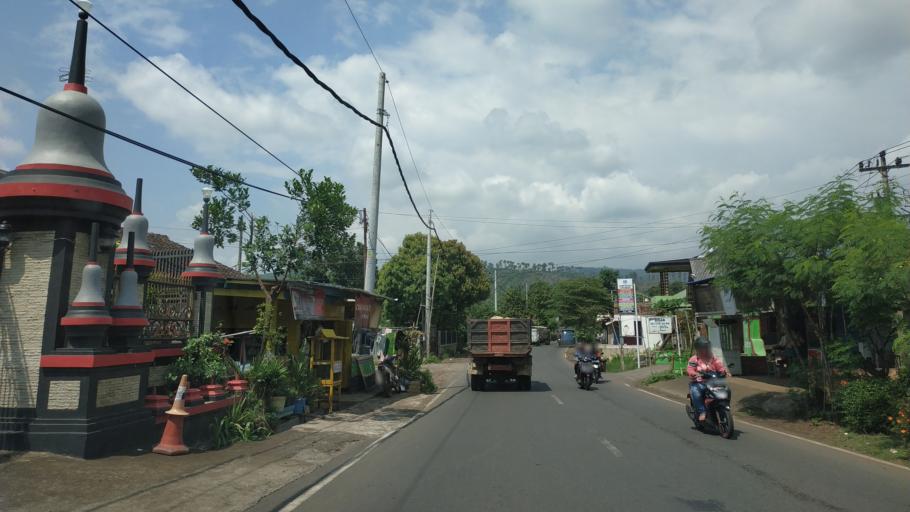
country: ID
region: Central Java
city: Weleri
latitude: -6.9969
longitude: 110.0723
